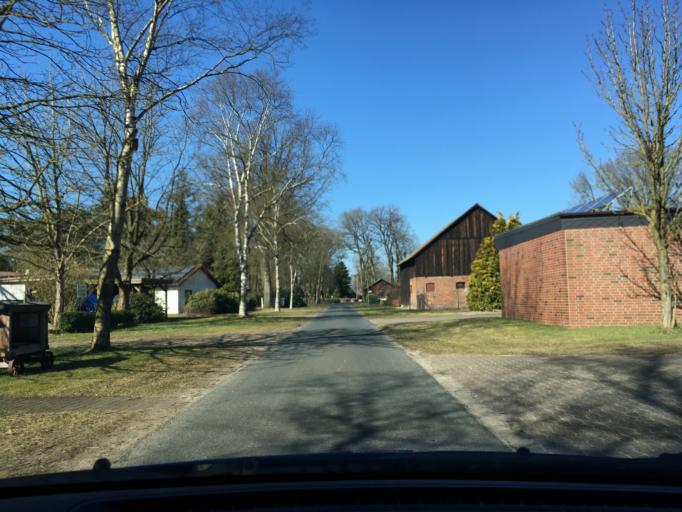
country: DE
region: Lower Saxony
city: Hemslingen
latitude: 53.0827
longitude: 9.6002
